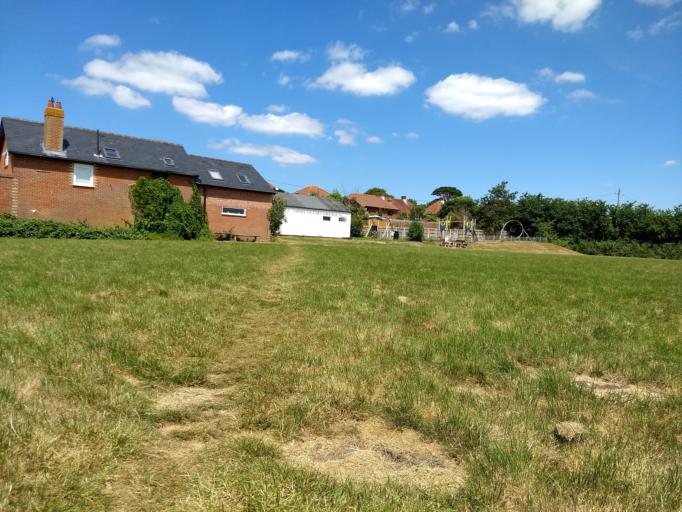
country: GB
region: England
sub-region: Isle of Wight
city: Yarmouth
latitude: 50.7042
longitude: -1.4954
